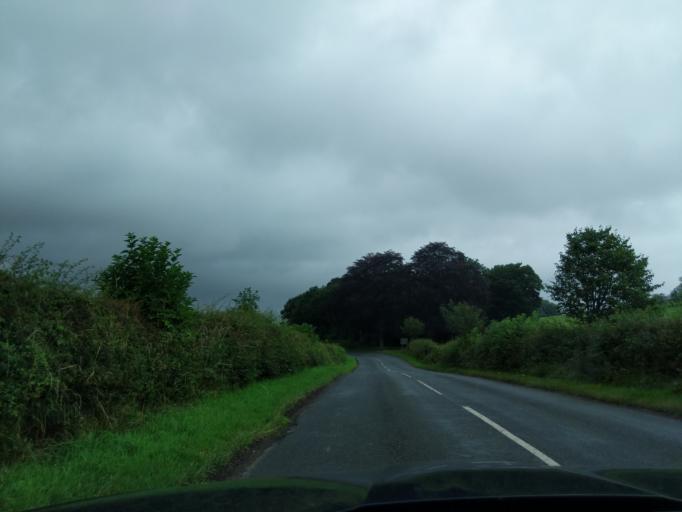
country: GB
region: England
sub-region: Northumberland
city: Ford
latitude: 55.6421
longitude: -2.1078
